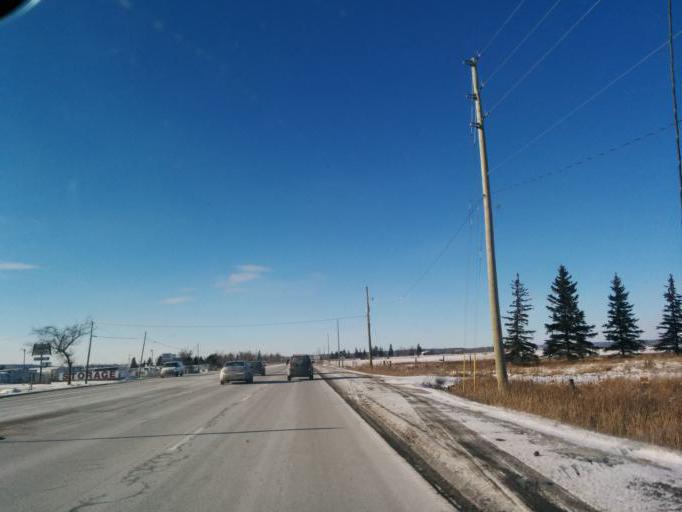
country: CA
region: Ontario
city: Brampton
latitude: 43.7565
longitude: -79.8484
